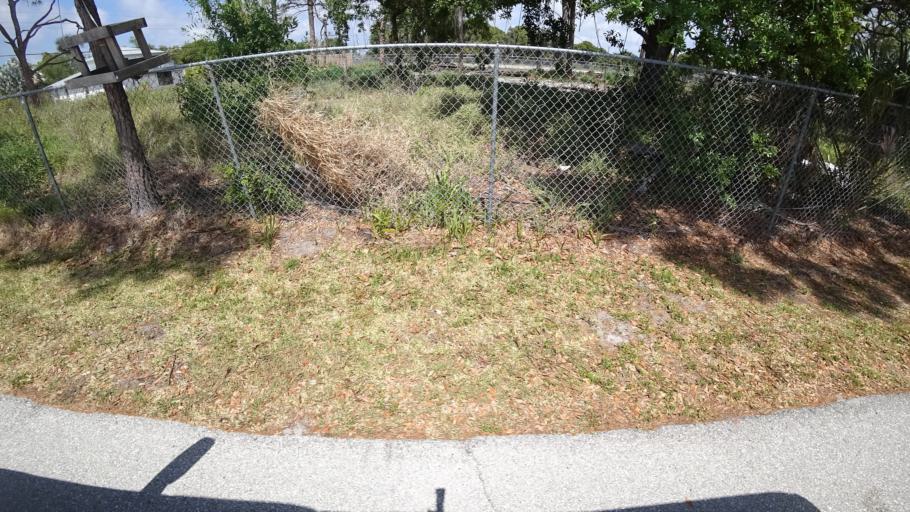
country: US
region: Florida
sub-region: Manatee County
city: Bayshore Gardens
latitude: 27.4257
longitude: -82.5793
